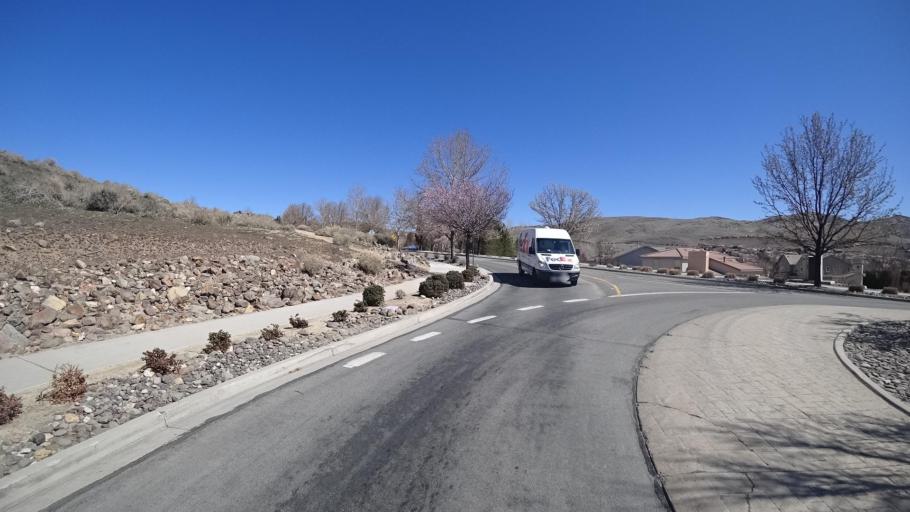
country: US
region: Nevada
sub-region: Washoe County
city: Sparks
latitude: 39.5577
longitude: -119.7034
